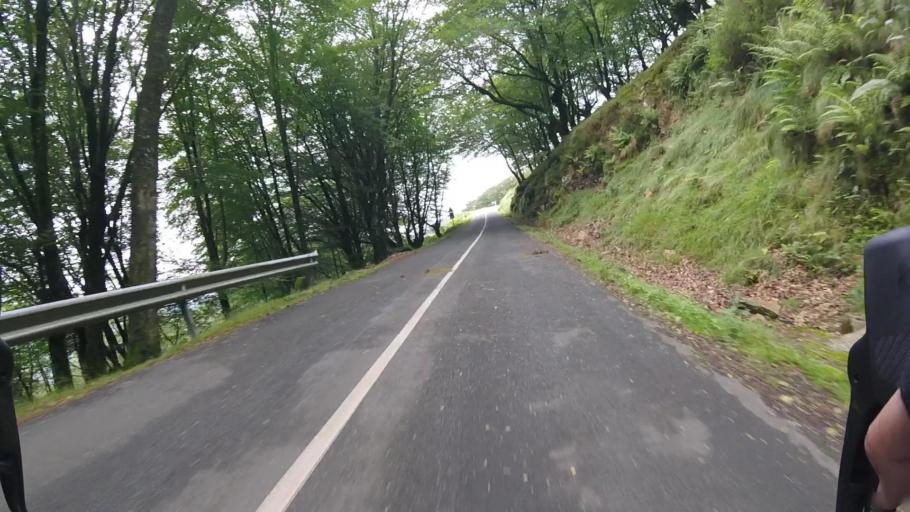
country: ES
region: Navarre
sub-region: Provincia de Navarra
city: Goizueta
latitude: 43.2468
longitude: -1.8163
